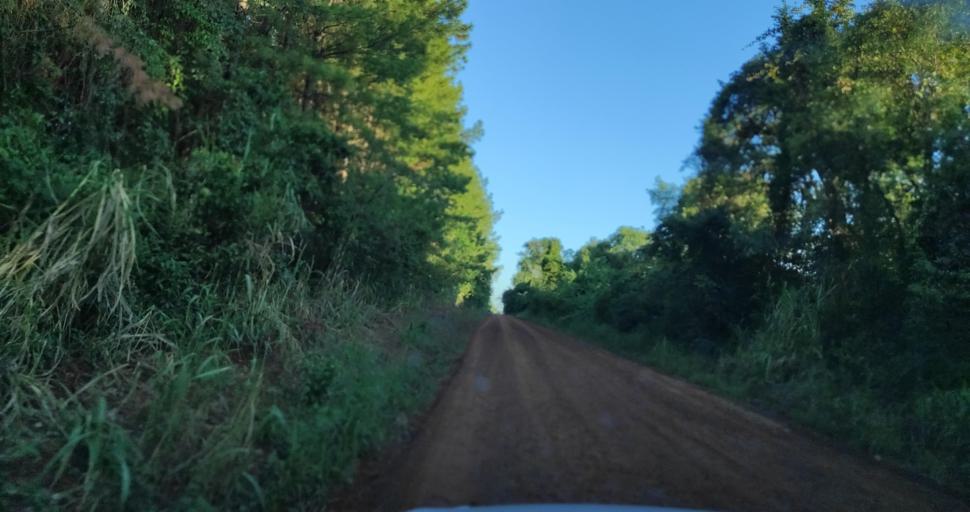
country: AR
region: Misiones
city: Gobernador Roca
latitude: -27.2197
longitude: -55.4369
